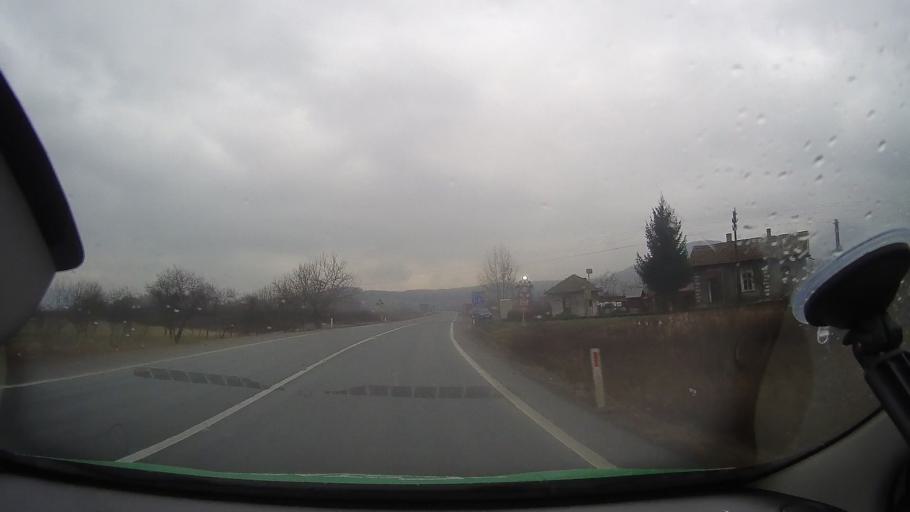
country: RO
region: Hunedoara
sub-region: Comuna Baia de Cris
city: Baia de Cris
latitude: 46.1807
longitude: 22.6808
